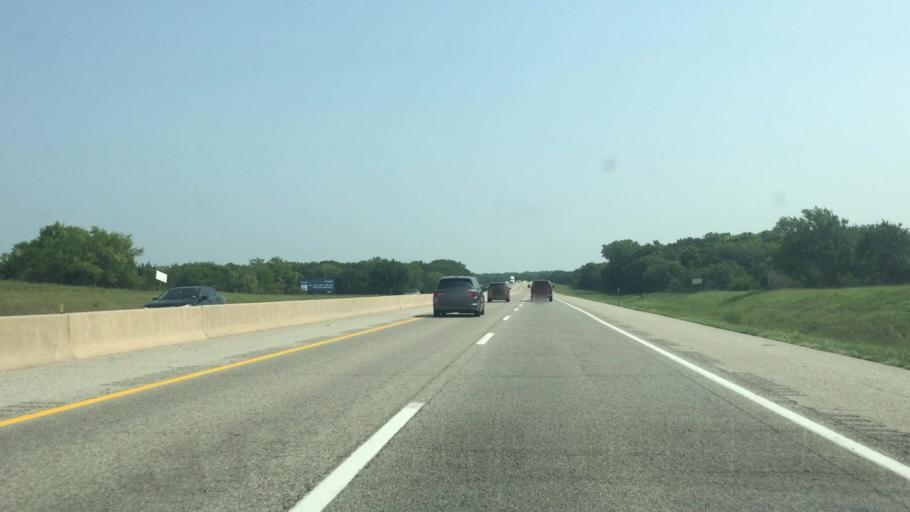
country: US
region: Kansas
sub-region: Lyon County
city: Emporia
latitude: 38.3632
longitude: -96.2776
